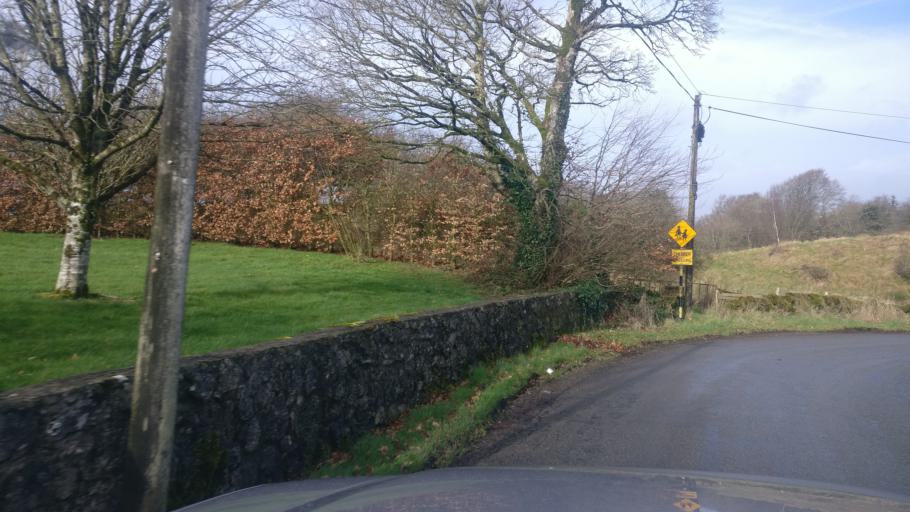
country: IE
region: Connaught
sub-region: County Galway
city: Loughrea
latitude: 53.2812
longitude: -8.5859
